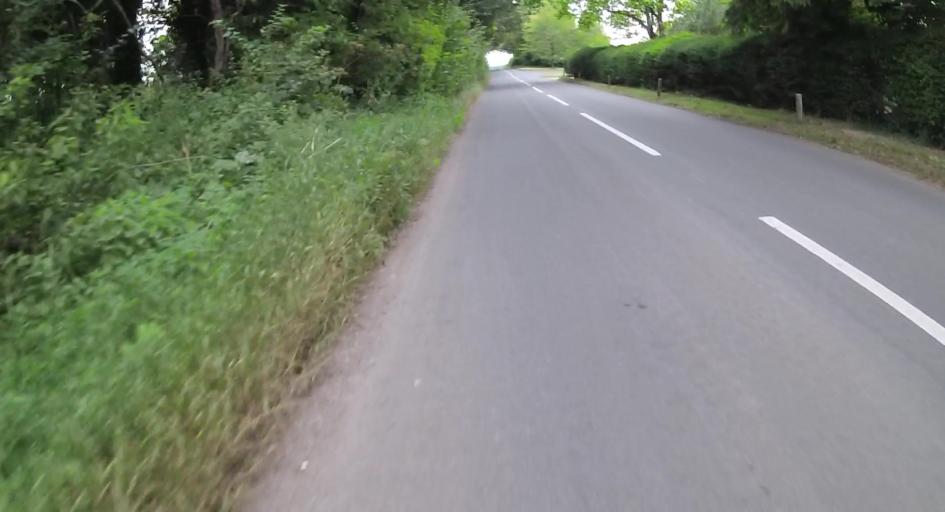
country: GB
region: England
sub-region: Hampshire
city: Kings Worthy
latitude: 51.1354
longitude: -1.3086
